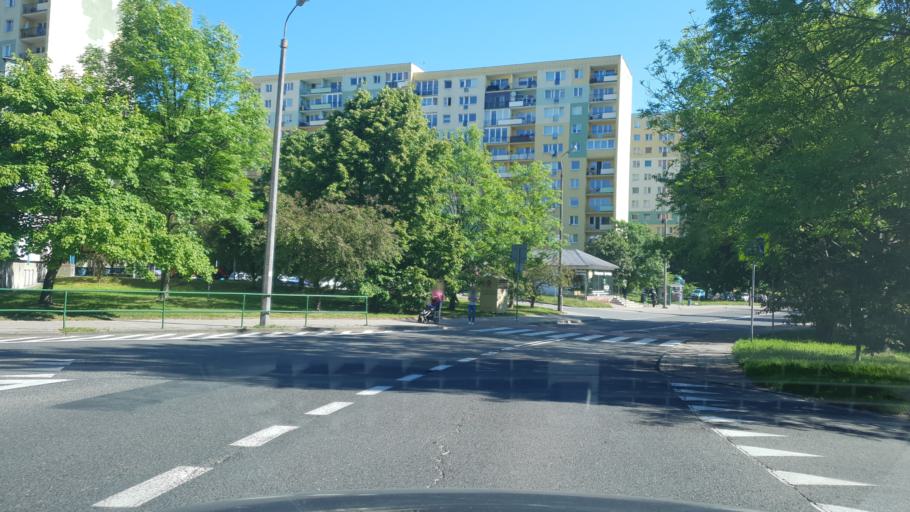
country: PL
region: Pomeranian Voivodeship
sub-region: Sopot
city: Sopot
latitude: 54.4570
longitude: 18.5335
